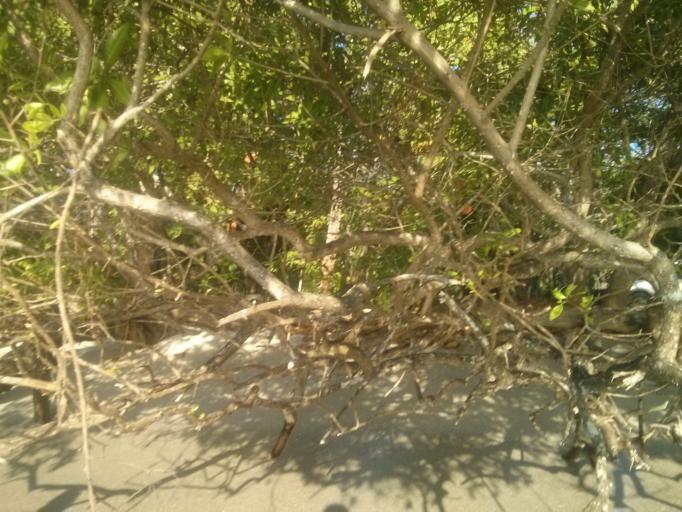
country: CR
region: Puntarenas
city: Paquera
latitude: 9.6196
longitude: -85.1466
